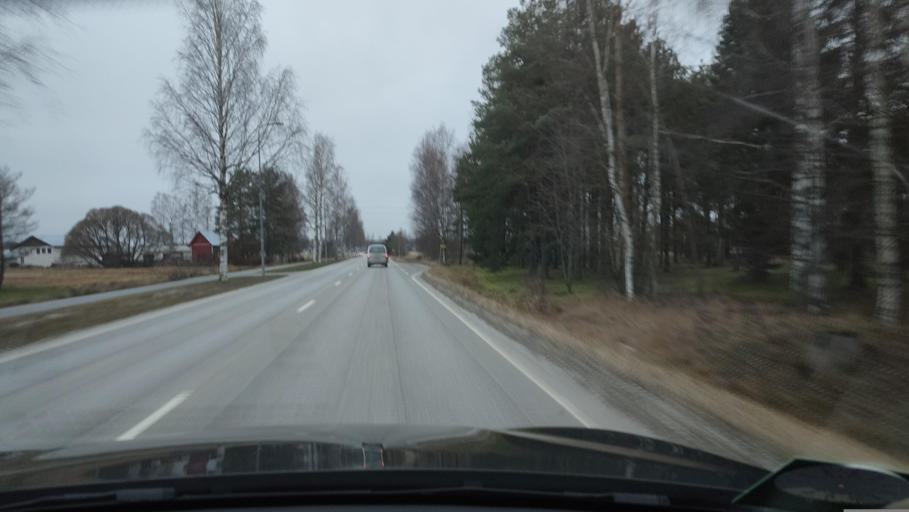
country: FI
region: Southern Ostrobothnia
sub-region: Suupohja
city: Kauhajoki
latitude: 62.4471
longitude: 22.2027
